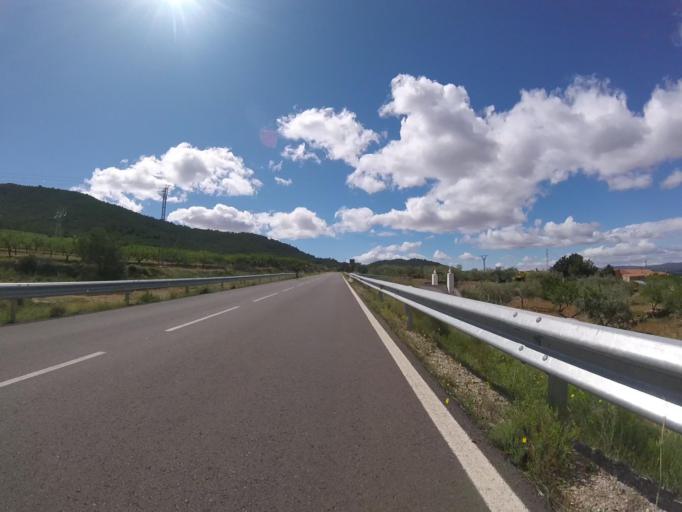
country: ES
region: Valencia
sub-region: Provincia de Castello
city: Culla
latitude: 40.2864
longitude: -0.1134
